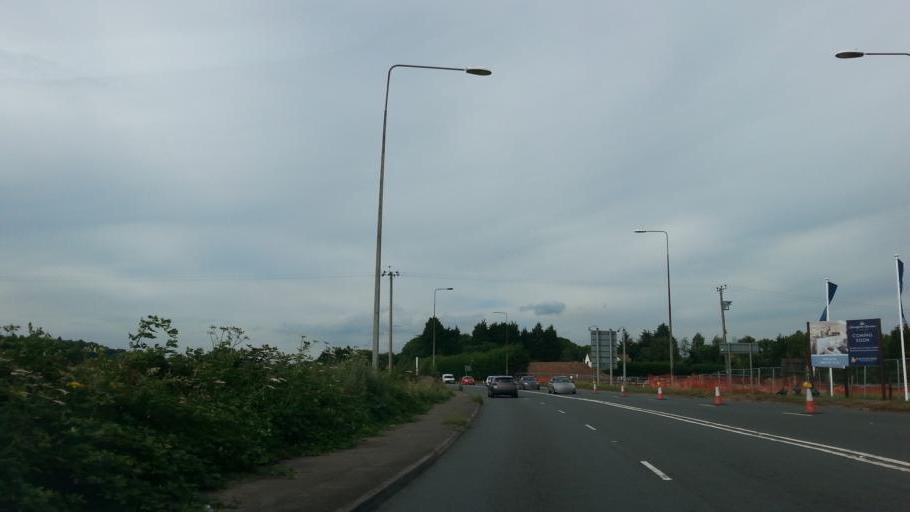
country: GB
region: Wales
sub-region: Newport
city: Marshfield
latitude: 51.5335
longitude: -3.0956
